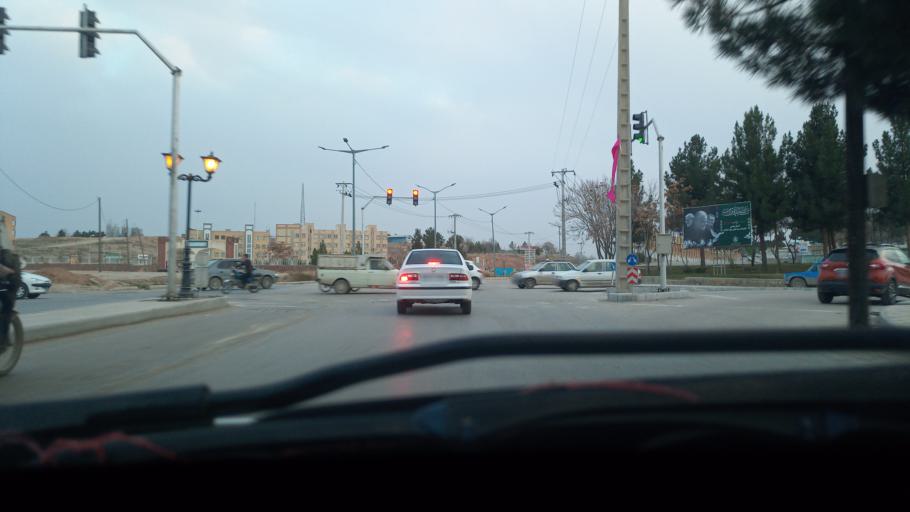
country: IR
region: Khorasan-e Shomali
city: Bojnurd
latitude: 37.4605
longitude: 57.3322
